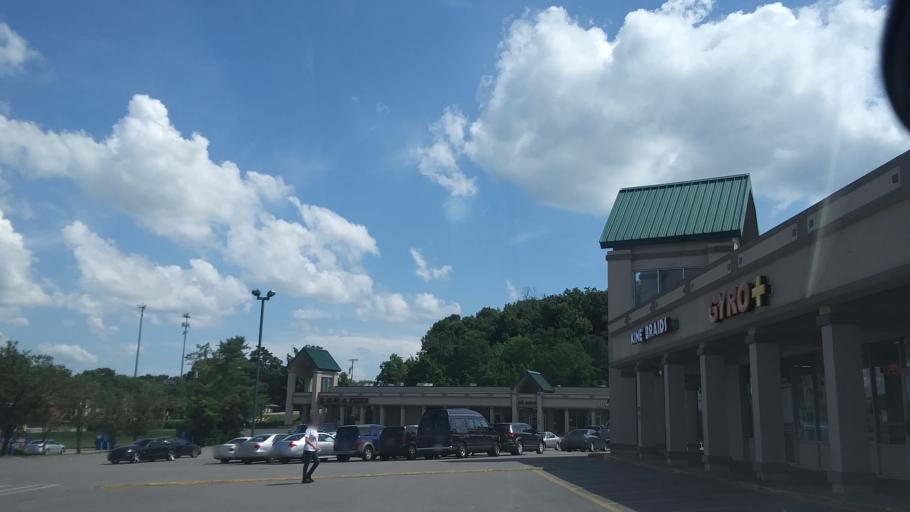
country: US
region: Tennessee
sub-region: Rutherford County
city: La Vergne
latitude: 36.0717
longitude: -86.6378
